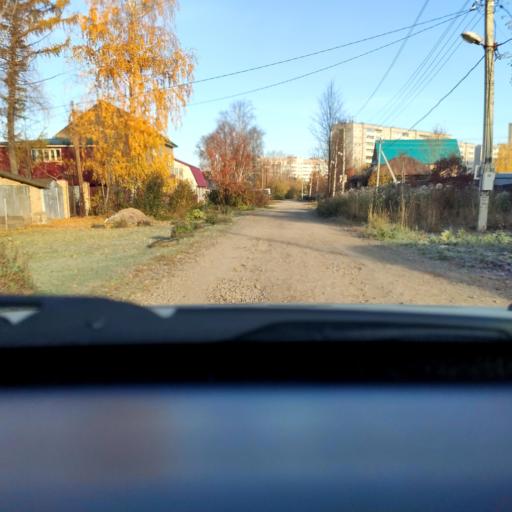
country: RU
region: Perm
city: Perm
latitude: 58.0262
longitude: 56.3265
